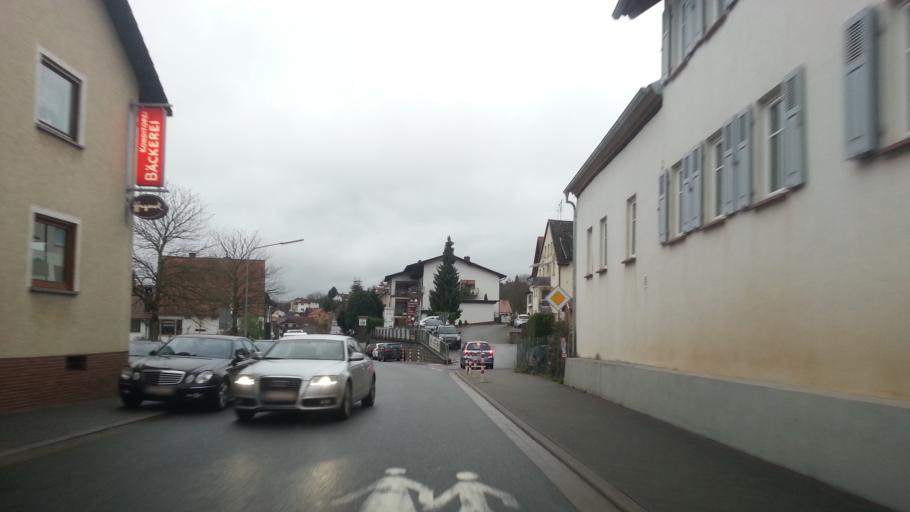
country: DE
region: Hesse
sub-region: Regierungsbezirk Darmstadt
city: Morlenbach
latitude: 49.5875
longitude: 8.7660
